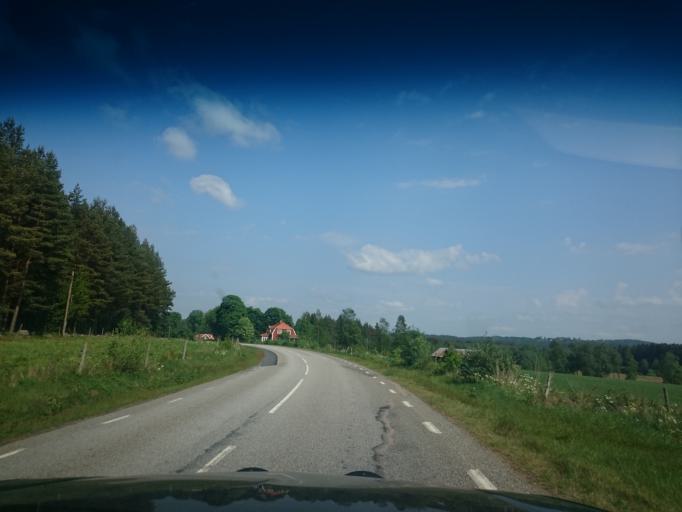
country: SE
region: Joenkoeping
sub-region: Vetlanda Kommun
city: Vetlanda
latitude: 57.3792
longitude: 14.9962
